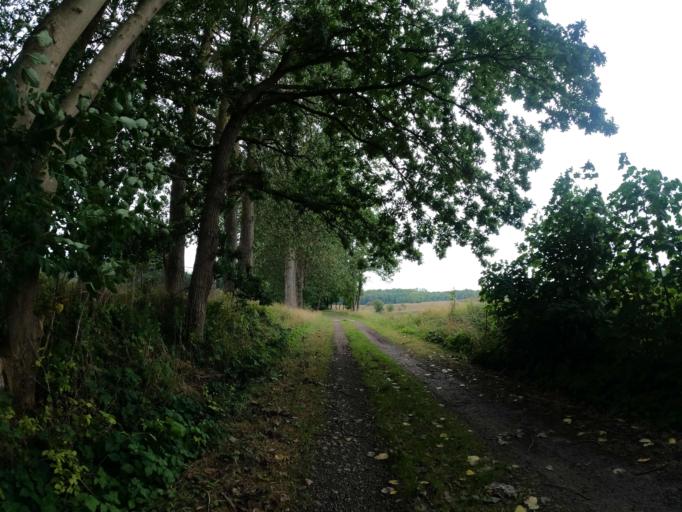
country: DE
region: Mecklenburg-Vorpommern
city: Putbus
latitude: 54.3587
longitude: 13.4608
